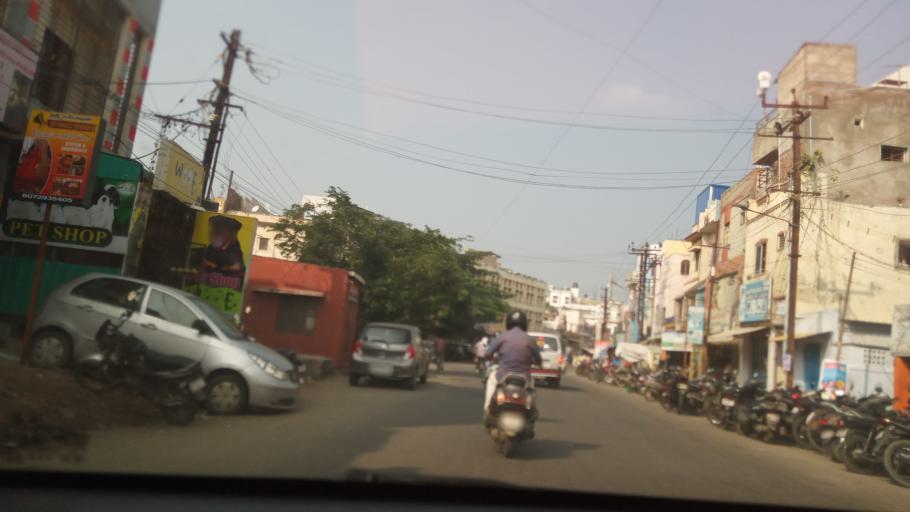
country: IN
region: Tamil Nadu
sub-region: Coimbatore
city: Coimbatore
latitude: 10.9996
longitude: 76.9516
